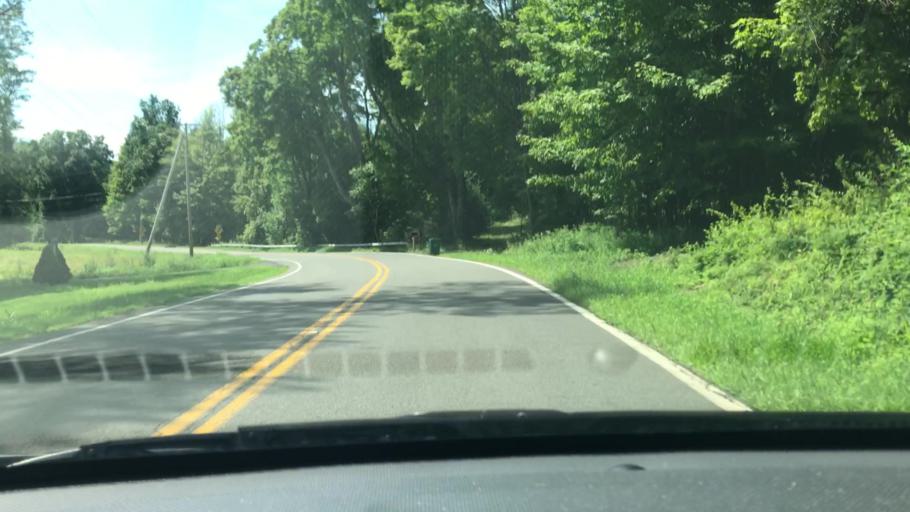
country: US
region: New York
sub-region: Ulster County
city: Shokan
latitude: 41.9243
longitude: -74.2148
